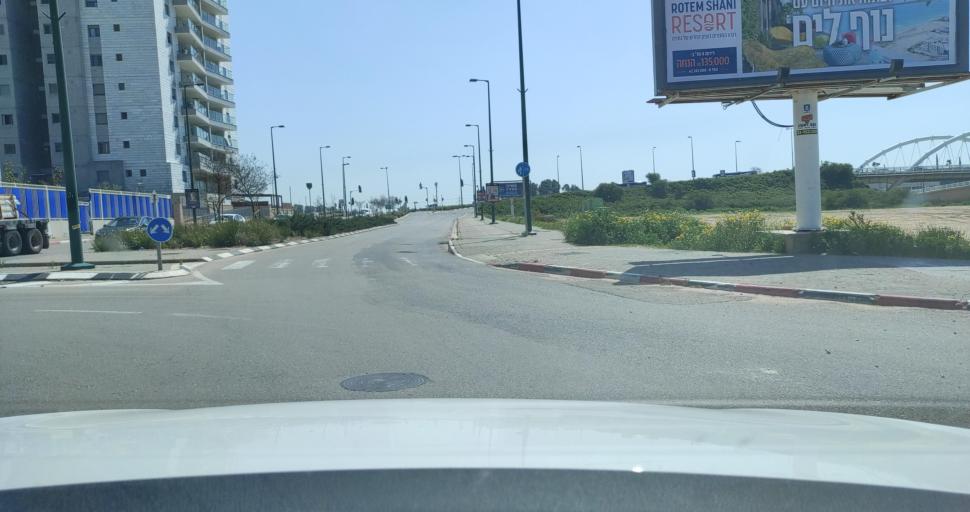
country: IL
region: Central District
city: Even Yehuda
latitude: 32.2947
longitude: 34.8691
